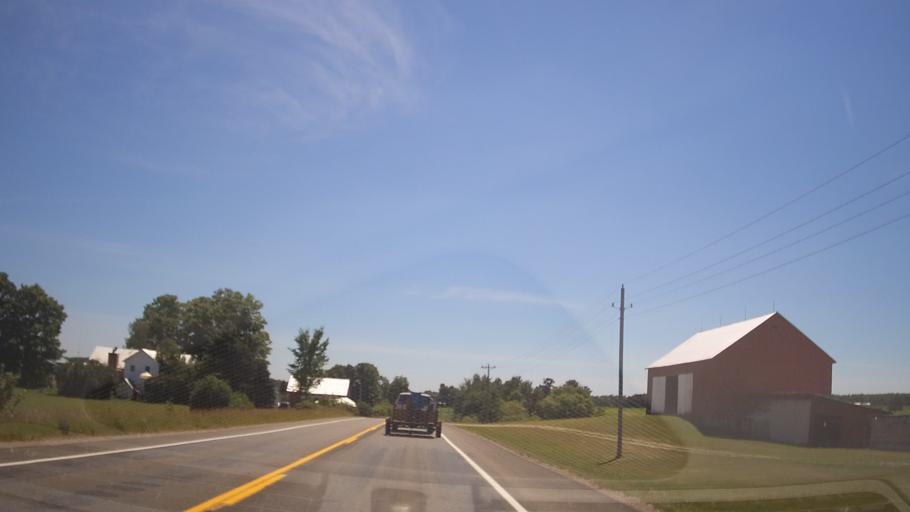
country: US
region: Michigan
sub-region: Grand Traverse County
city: Kingsley
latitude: 44.6074
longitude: -85.6965
